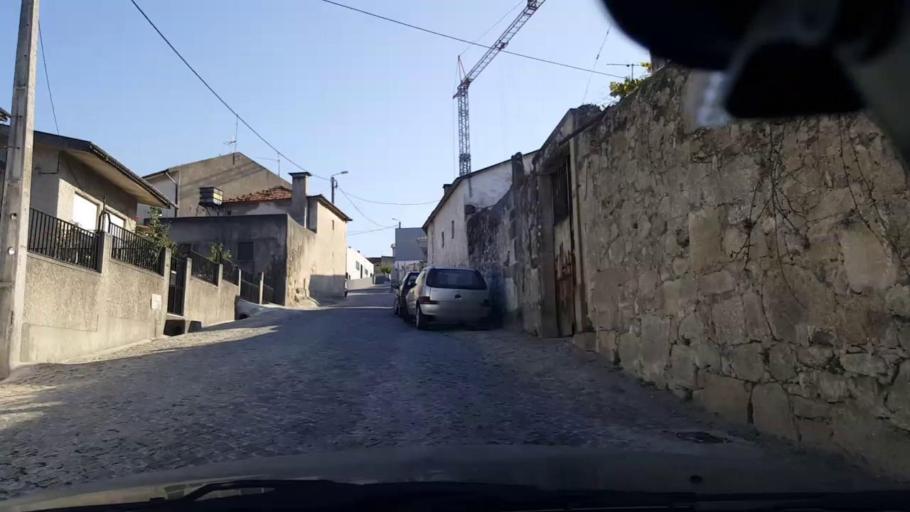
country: PT
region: Porto
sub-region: Vila do Conde
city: Arvore
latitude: 41.3565
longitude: -8.7223
